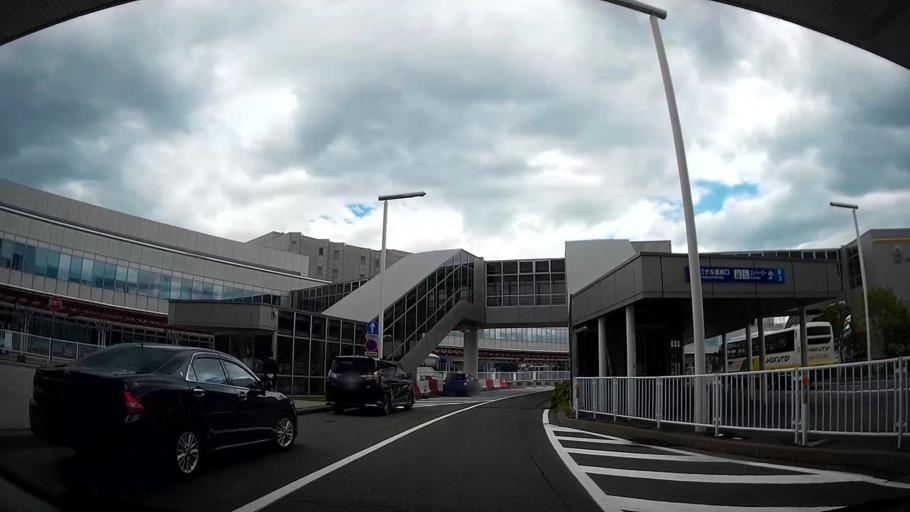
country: JP
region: Hokkaido
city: Chitose
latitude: 42.7867
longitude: 141.6807
